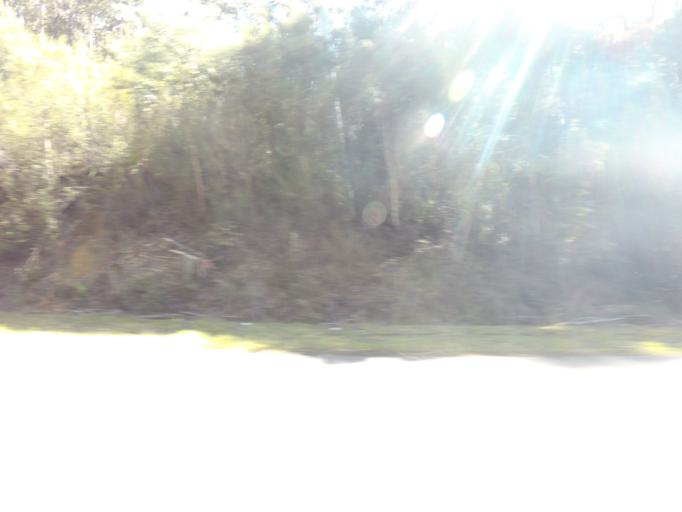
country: AU
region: Tasmania
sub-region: Derwent Valley
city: New Norfolk
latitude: -42.7405
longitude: 146.4963
